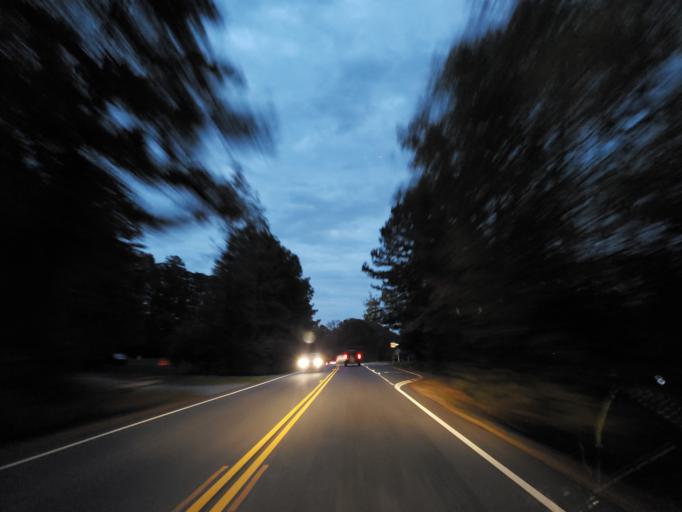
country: US
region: Georgia
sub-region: Cobb County
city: Powder Springs
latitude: 33.9119
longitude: -84.6860
